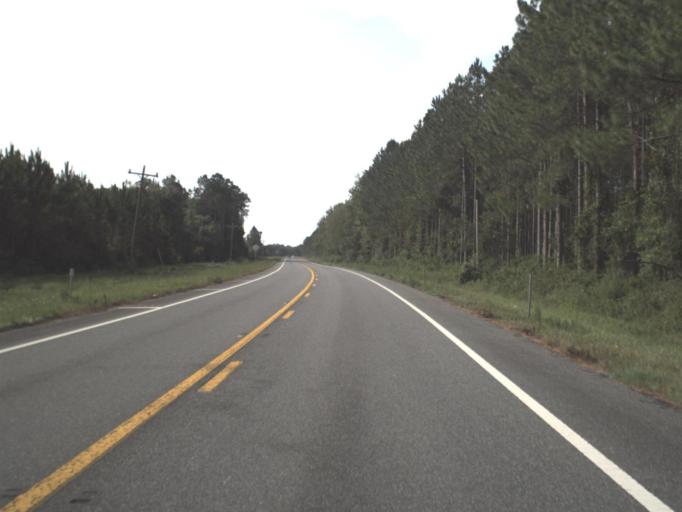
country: US
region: Florida
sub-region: Taylor County
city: Perry
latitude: 30.2133
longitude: -83.6124
